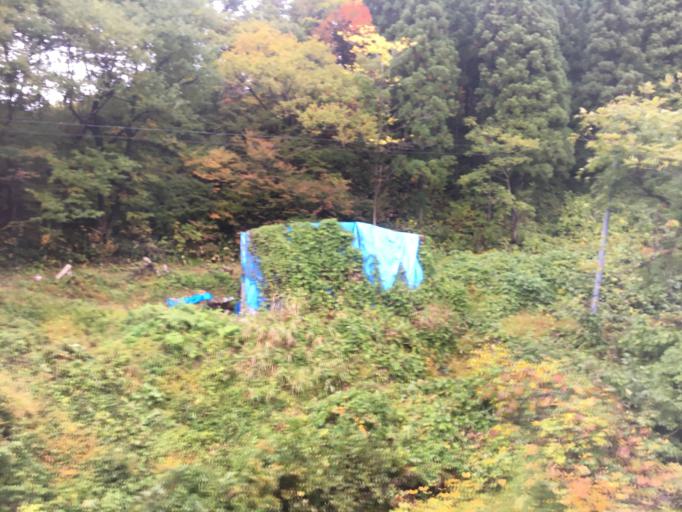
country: JP
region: Yamagata
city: Nagai
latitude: 38.0149
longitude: 139.8963
